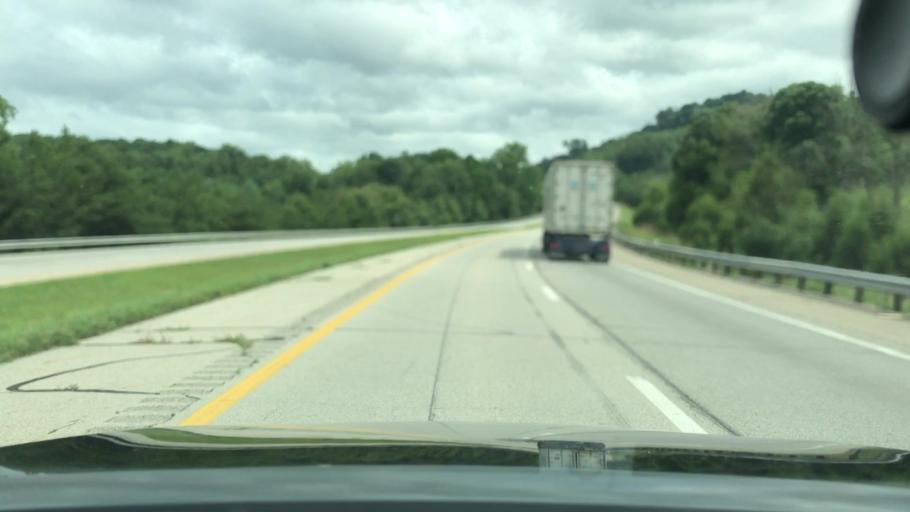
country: US
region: Ohio
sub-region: Jackson County
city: Jackson
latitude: 39.1149
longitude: -82.6820
